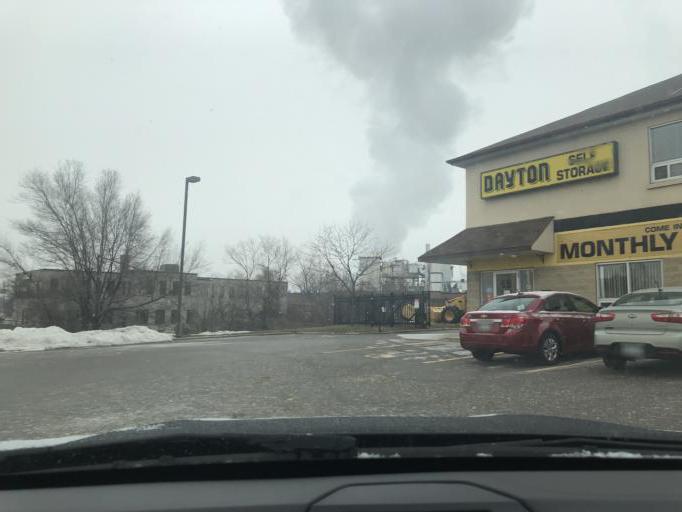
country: CA
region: Ontario
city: Scarborough
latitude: 43.7709
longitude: -79.2766
